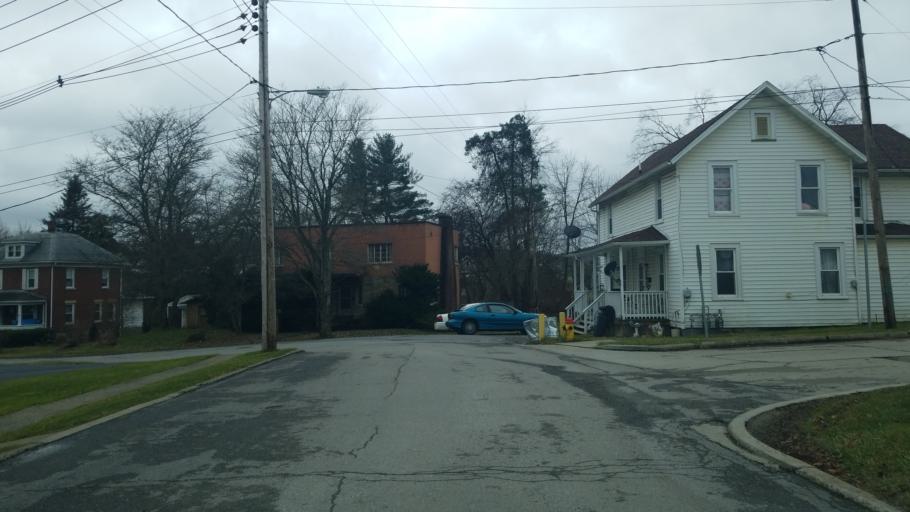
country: US
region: Pennsylvania
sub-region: Clearfield County
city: Sandy
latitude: 41.1131
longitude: -78.7725
